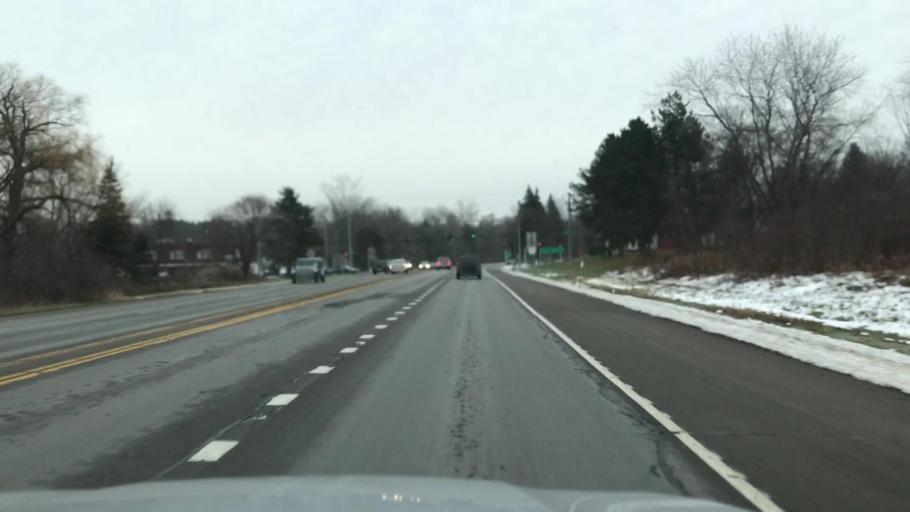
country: US
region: New York
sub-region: Erie County
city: Orchard Park
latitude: 42.7489
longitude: -78.7500
